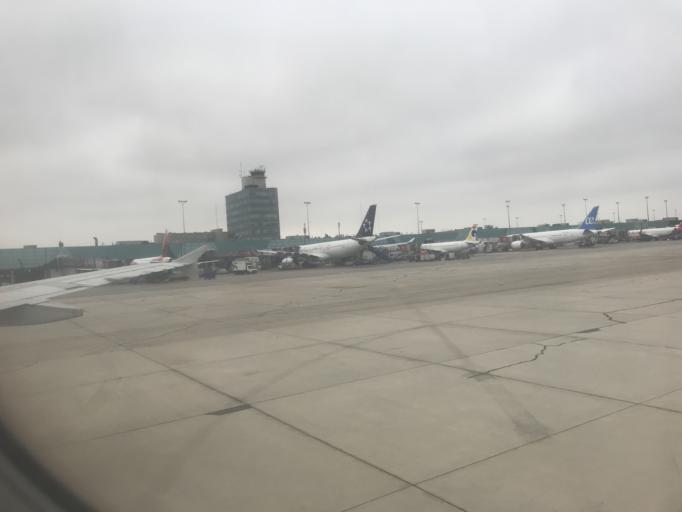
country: PE
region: Callao
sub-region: Callao
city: Callao
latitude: -12.0234
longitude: -77.1111
